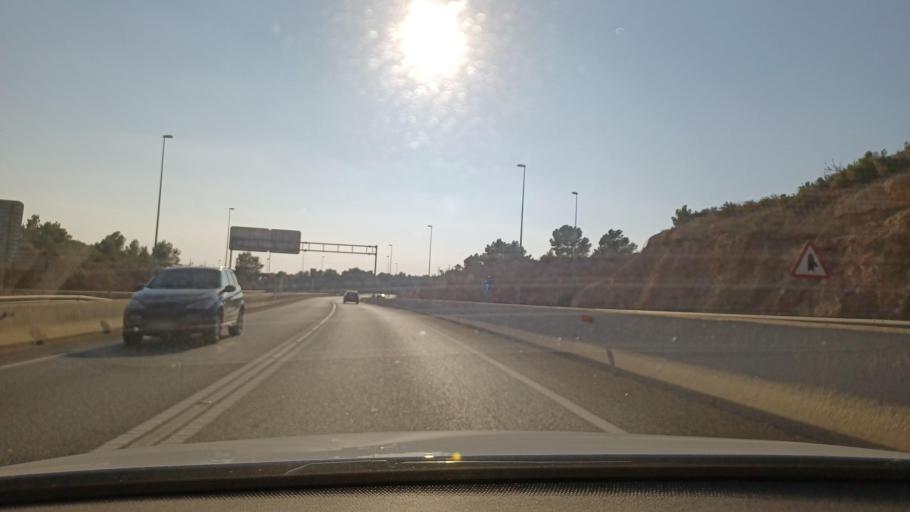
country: ES
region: Catalonia
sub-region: Provincia de Tarragona
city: l'Ametlla de Mar
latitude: 40.9506
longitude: 0.8568
